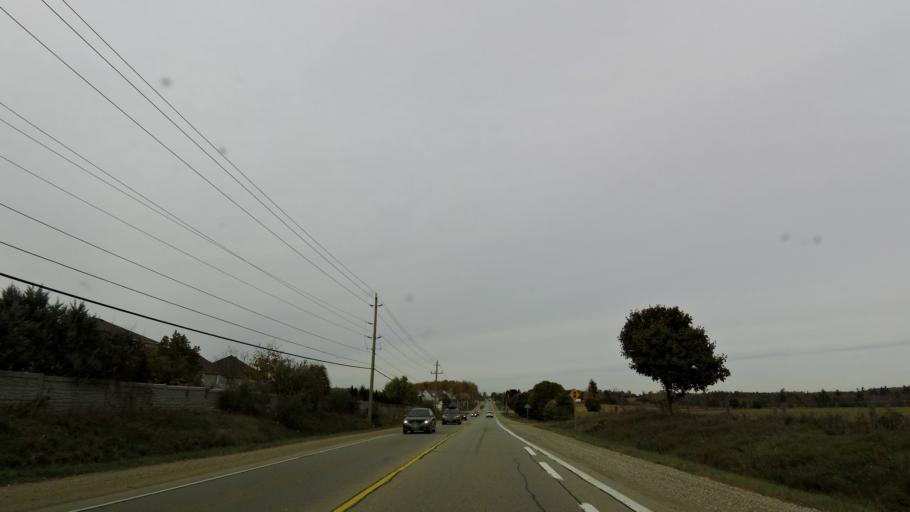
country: CA
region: Ontario
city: Cambridge
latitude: 43.4271
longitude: -80.2857
